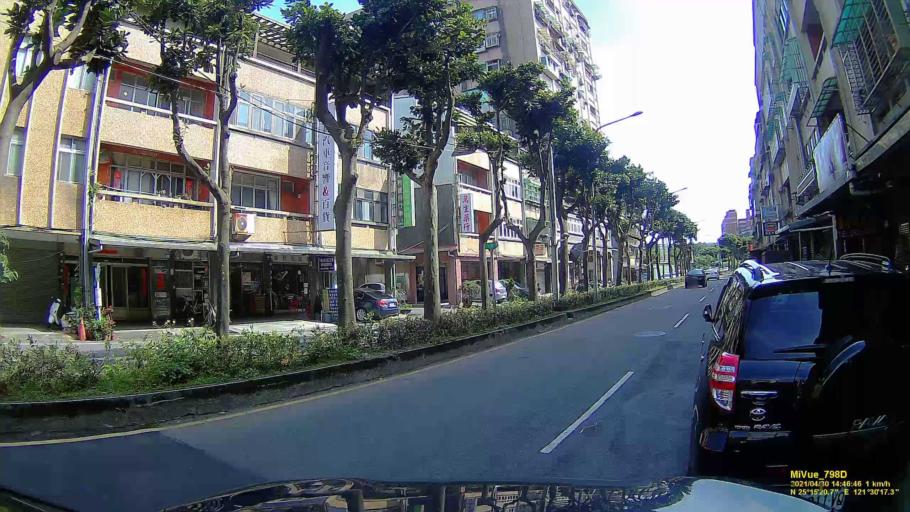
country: TW
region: Taipei
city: Taipei
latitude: 25.2557
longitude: 121.5047
